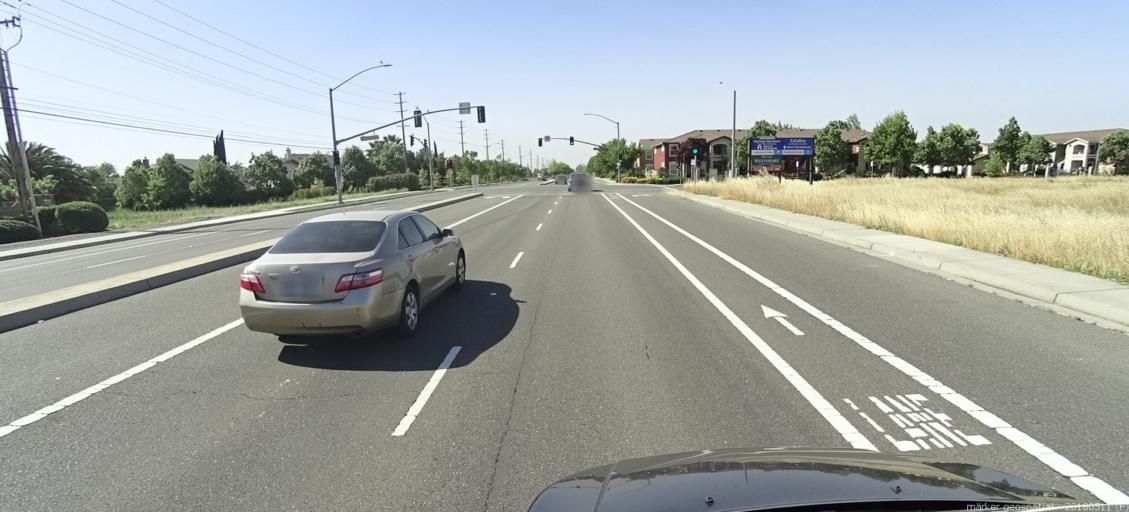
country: US
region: California
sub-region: Yolo County
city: West Sacramento
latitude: 38.6497
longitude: -121.5398
